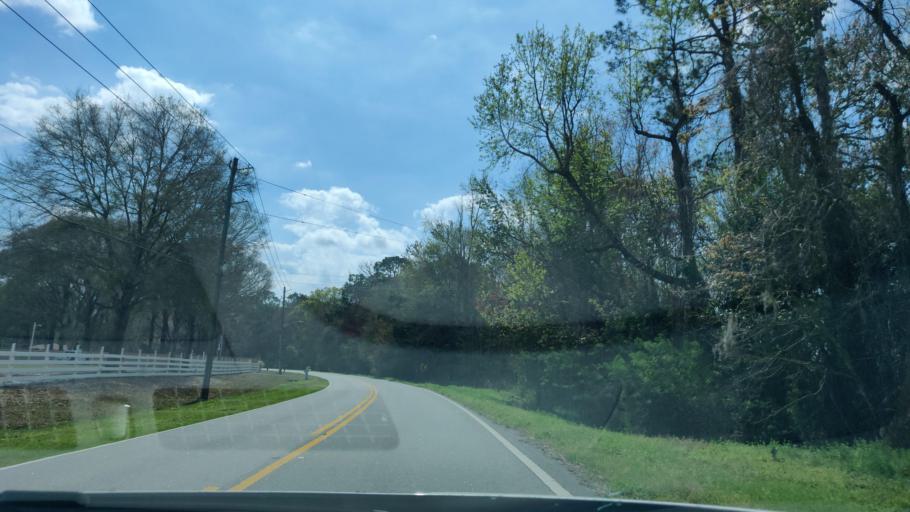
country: US
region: Florida
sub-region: Duval County
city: Baldwin
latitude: 30.2486
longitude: -81.9492
